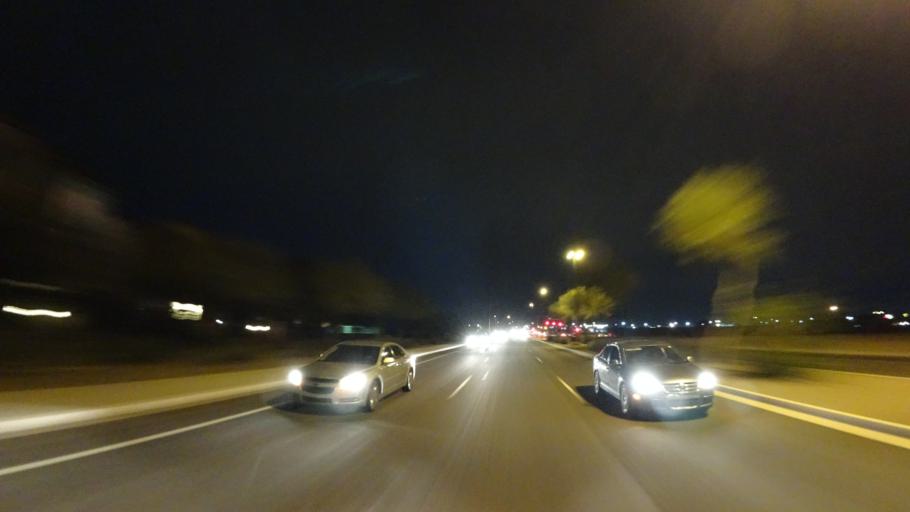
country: US
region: Arizona
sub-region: Maricopa County
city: Gilbert
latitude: 33.3067
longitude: -111.7367
